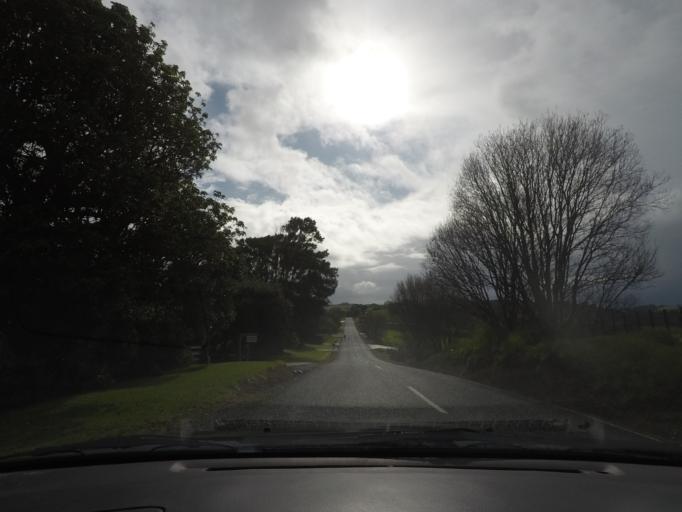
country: NZ
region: Auckland
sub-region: Auckland
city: Warkworth
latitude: -36.4716
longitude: 174.7345
